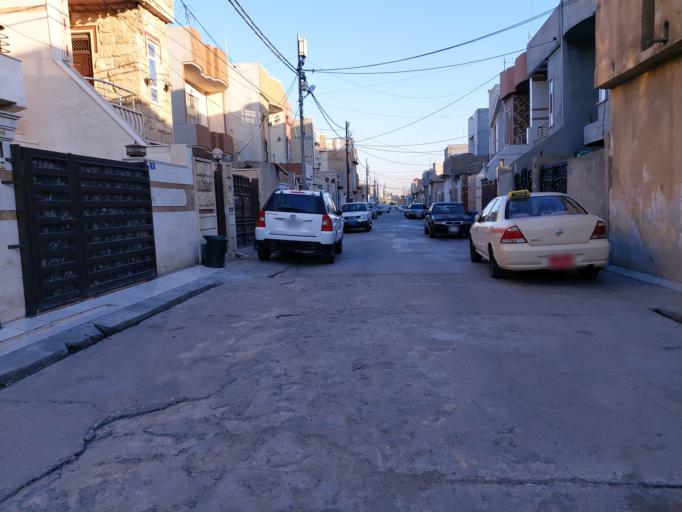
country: IQ
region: Arbil
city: Erbil
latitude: 36.1594
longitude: 43.9914
